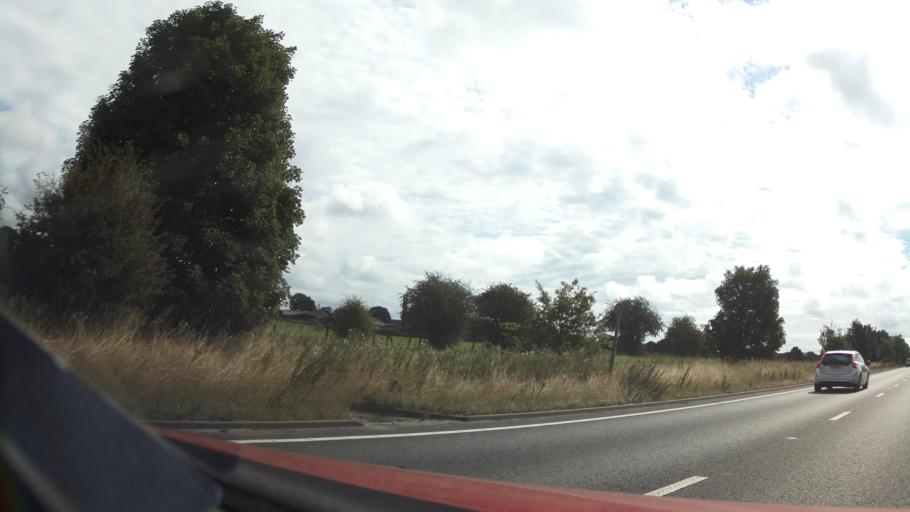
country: GB
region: England
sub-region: Derbyshire
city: Alfreton
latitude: 53.0812
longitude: -1.4092
